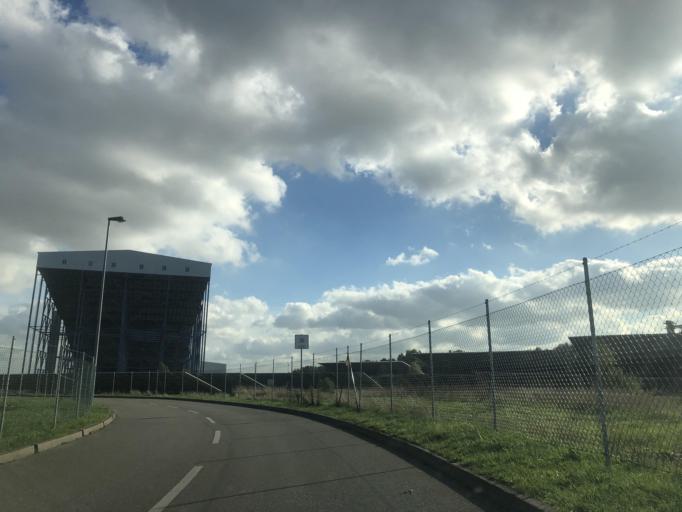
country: DE
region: Mecklenburg-Vorpommern
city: Wittenburg
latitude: 53.5112
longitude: 11.0880
